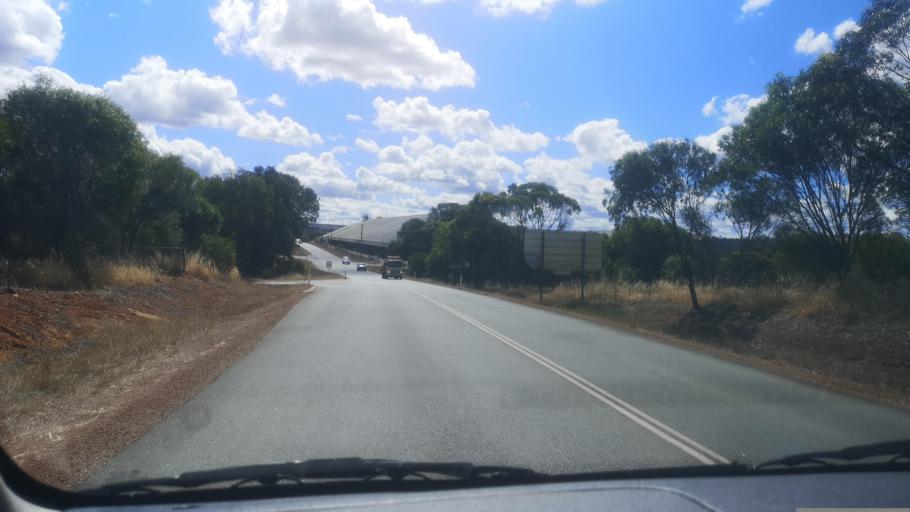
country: AU
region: Western Australia
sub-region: Northam
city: Northam
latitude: -31.6424
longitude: 116.6401
